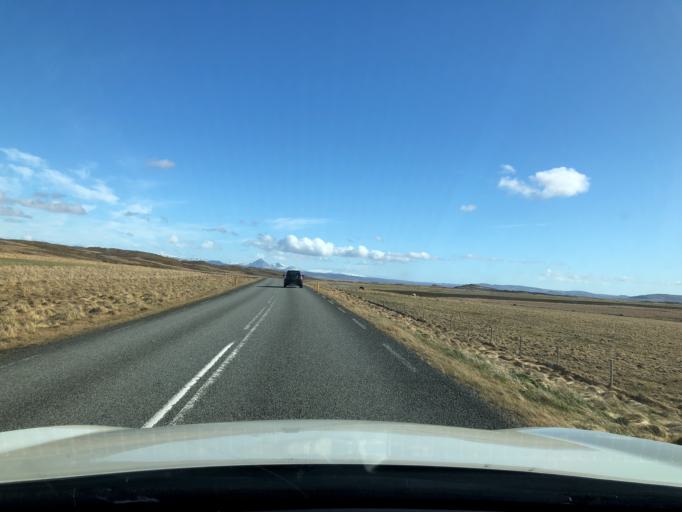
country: IS
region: West
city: Borgarnes
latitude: 64.5753
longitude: -21.6536
